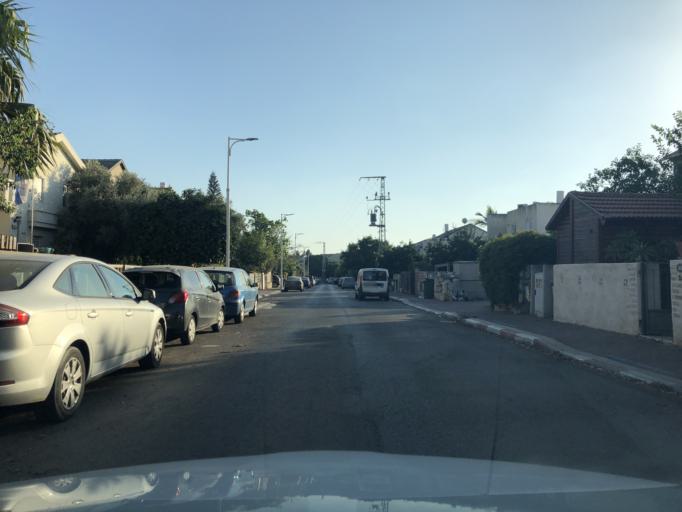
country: PS
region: West Bank
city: Hablah
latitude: 32.1633
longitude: 34.9705
